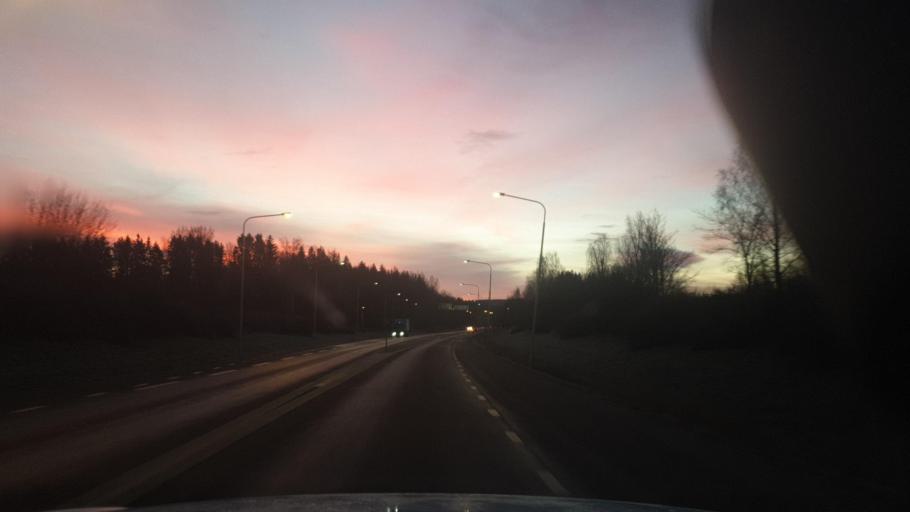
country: SE
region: Vaermland
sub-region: Arvika Kommun
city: Arvika
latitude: 59.6674
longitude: 12.6078
